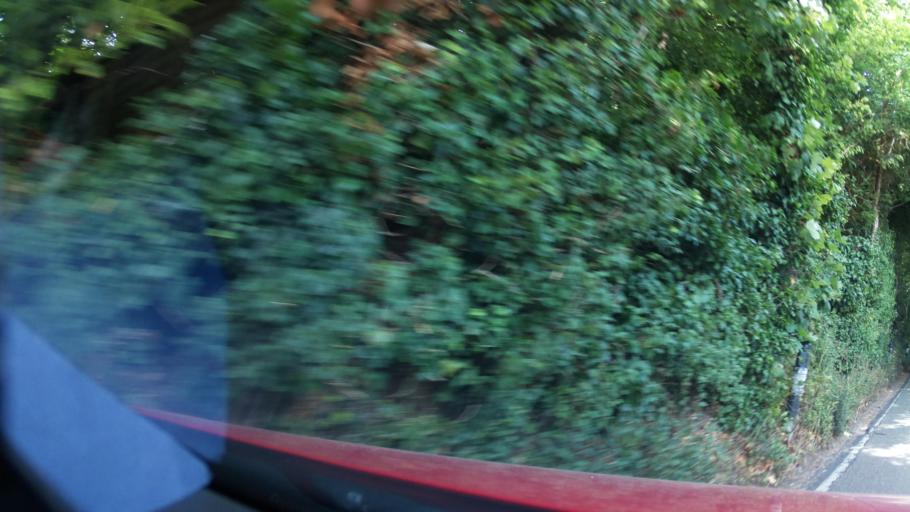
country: GB
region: England
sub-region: Surrey
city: Chilworth
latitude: 51.2430
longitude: -0.5255
